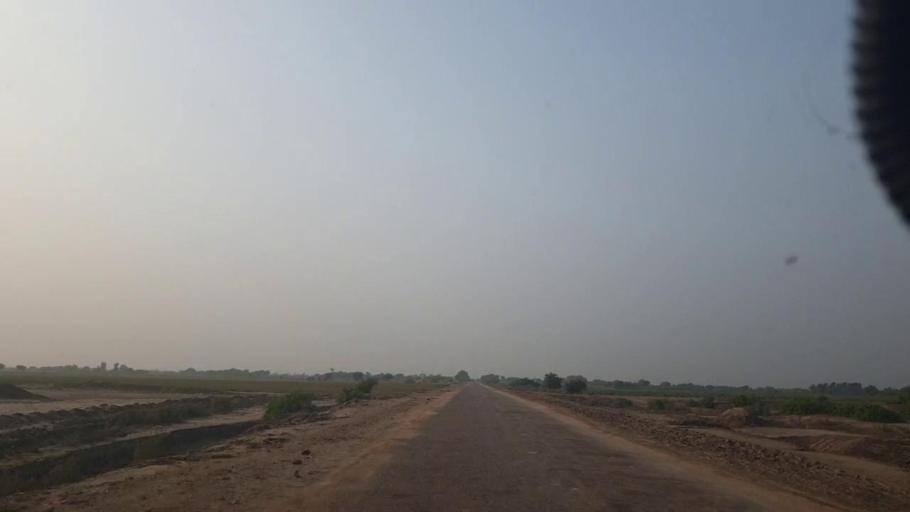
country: PK
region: Sindh
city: Bulri
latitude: 24.8583
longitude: 68.3994
